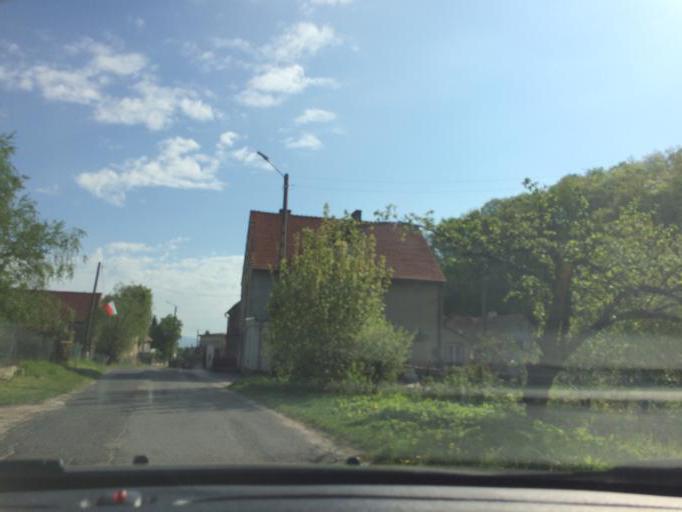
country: PL
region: Lower Silesian Voivodeship
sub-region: Powiat walbrzyski
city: Walim
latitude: 50.7464
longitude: 16.4953
